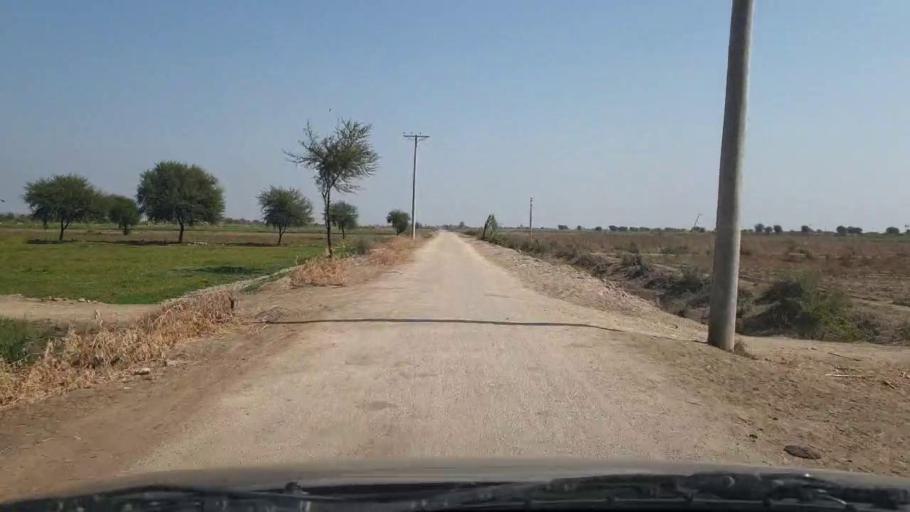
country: PK
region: Sindh
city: Samaro
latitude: 25.1995
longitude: 69.2905
